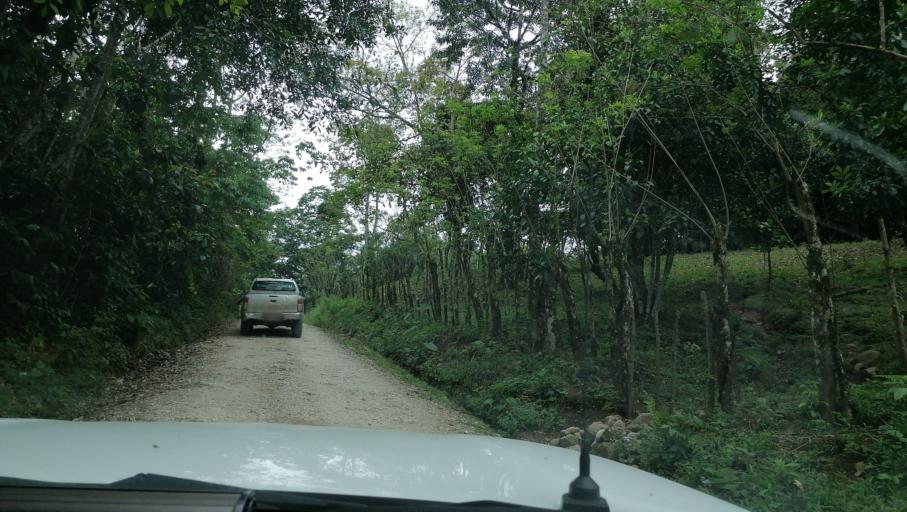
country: MX
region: Chiapas
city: Ocotepec
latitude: 17.2751
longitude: -93.2236
